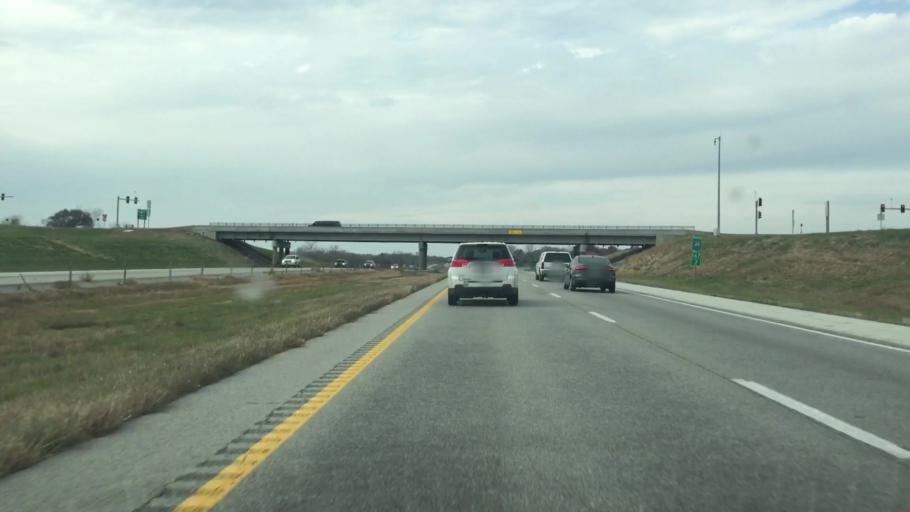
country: US
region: Missouri
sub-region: Cass County
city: Peculiar
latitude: 38.7220
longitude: -94.4539
